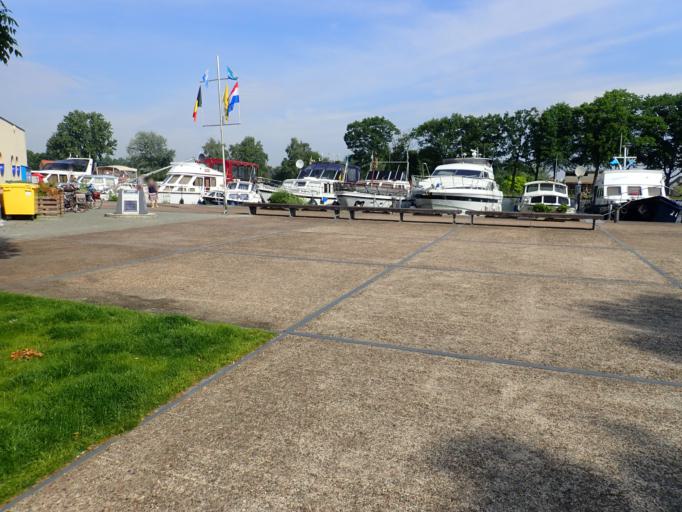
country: BE
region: Flanders
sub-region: Provincie Antwerpen
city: Turnhout
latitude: 51.3261
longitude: 4.9322
